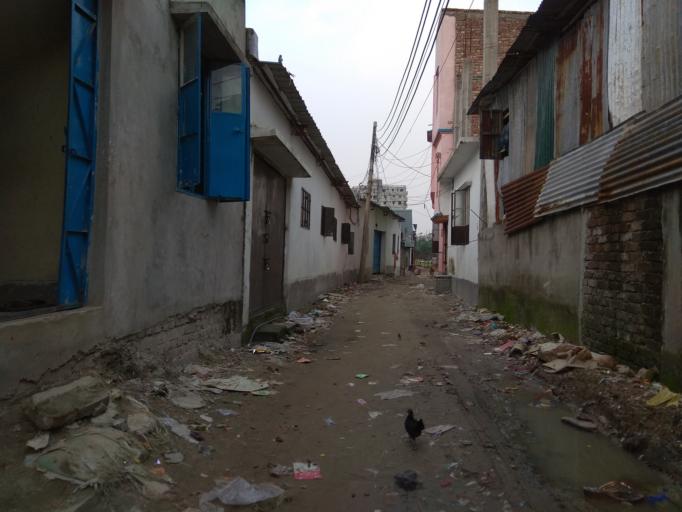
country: BD
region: Dhaka
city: Tungi
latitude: 23.8145
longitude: 90.3831
